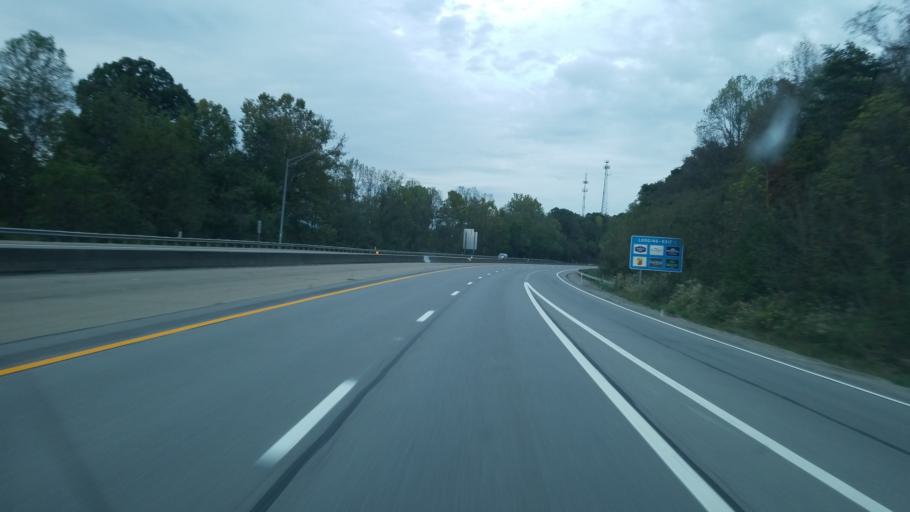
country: US
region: West Virginia
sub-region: Wood County
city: Williamstown
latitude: 39.3922
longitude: -81.4393
